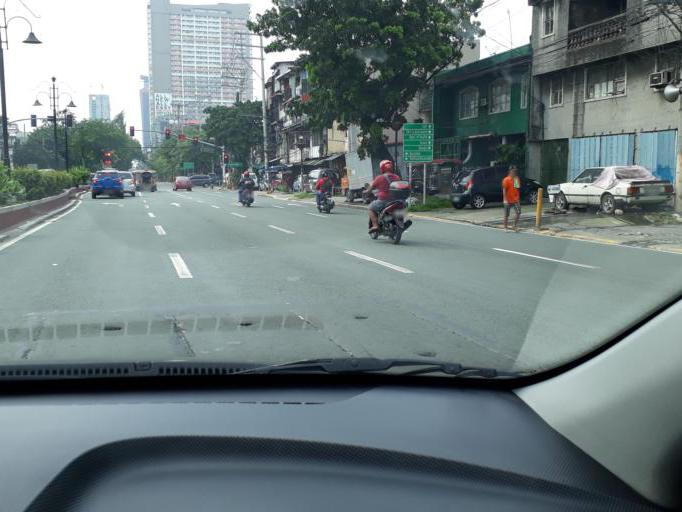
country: PH
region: Metro Manila
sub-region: City of Manila
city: Manila
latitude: 14.6069
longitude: 120.9955
